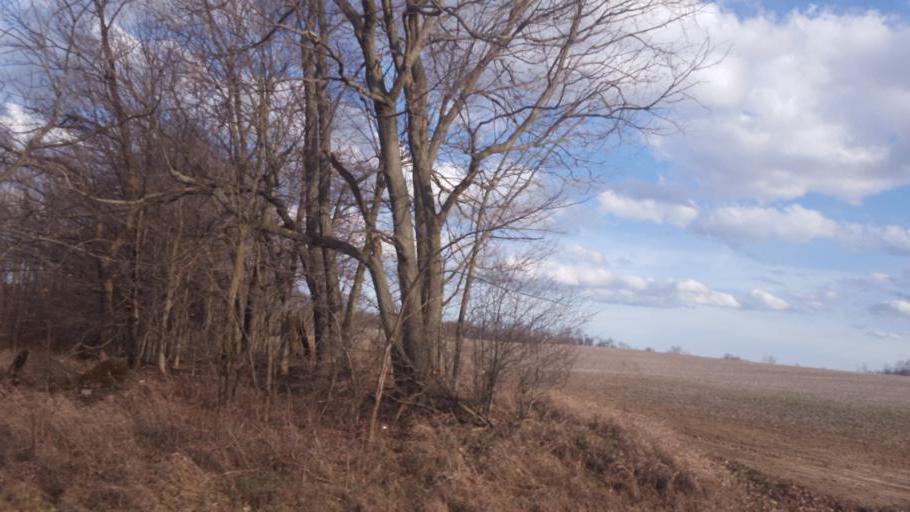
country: US
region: Ohio
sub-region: Sandusky County
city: Bellville
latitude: 40.5435
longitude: -82.4498
